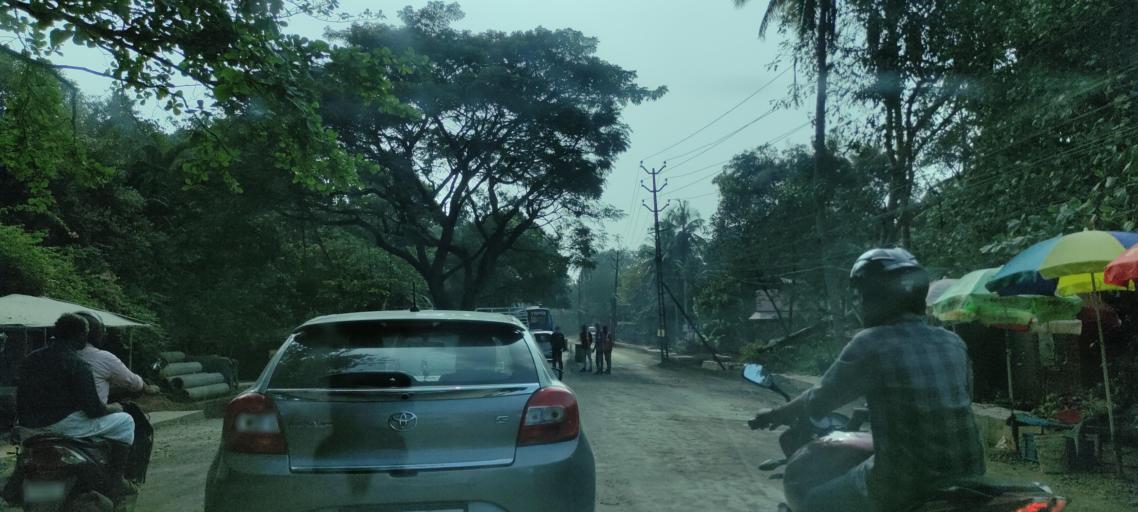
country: IN
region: Kerala
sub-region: Pattanamtitta
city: Tiruvalla
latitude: 9.3691
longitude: 76.5482
